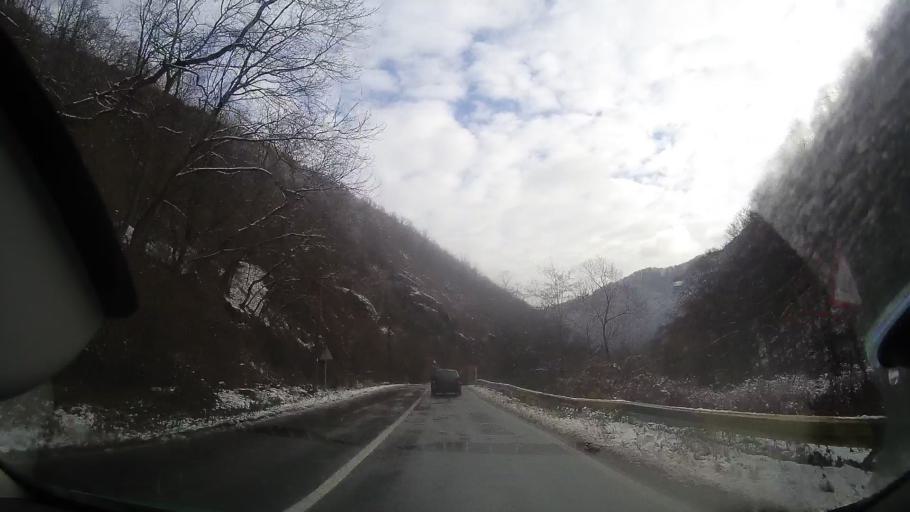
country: RO
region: Alba
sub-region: Oras Baia de Aries
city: Baia de Aries
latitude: 46.4043
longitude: 23.3391
